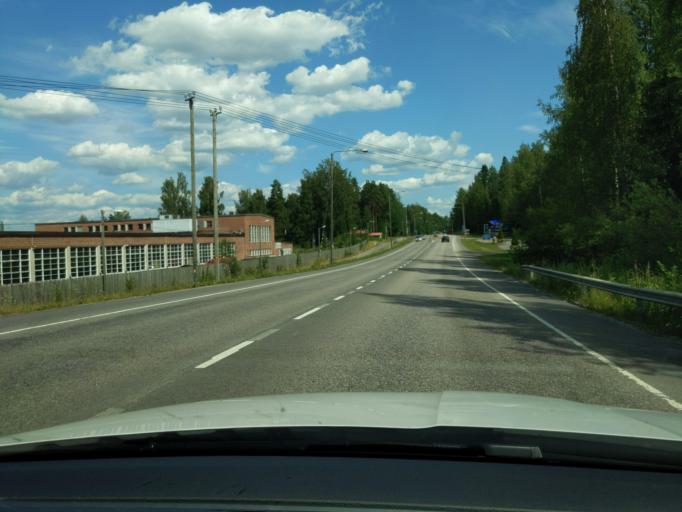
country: FI
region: Paijanne Tavastia
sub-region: Lahti
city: Heinola
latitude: 61.1935
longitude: 26.0088
